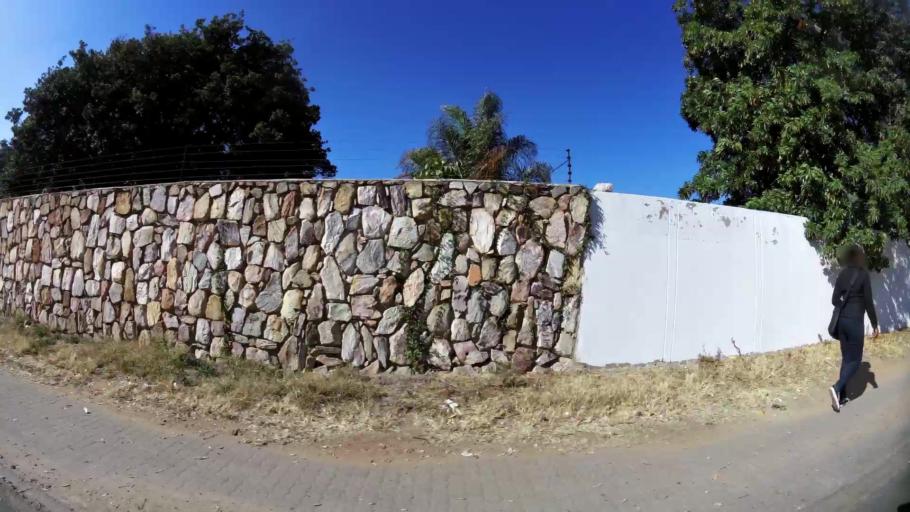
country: ZA
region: Gauteng
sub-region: City of Johannesburg Metropolitan Municipality
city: Modderfontein
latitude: -26.1218
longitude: 28.0920
